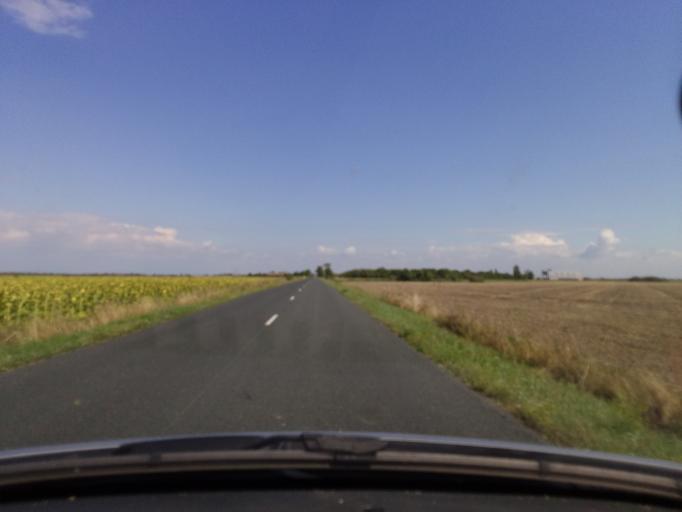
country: FR
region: Pays de la Loire
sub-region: Departement de la Vendee
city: Triaize
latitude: 46.4009
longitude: -1.2395
